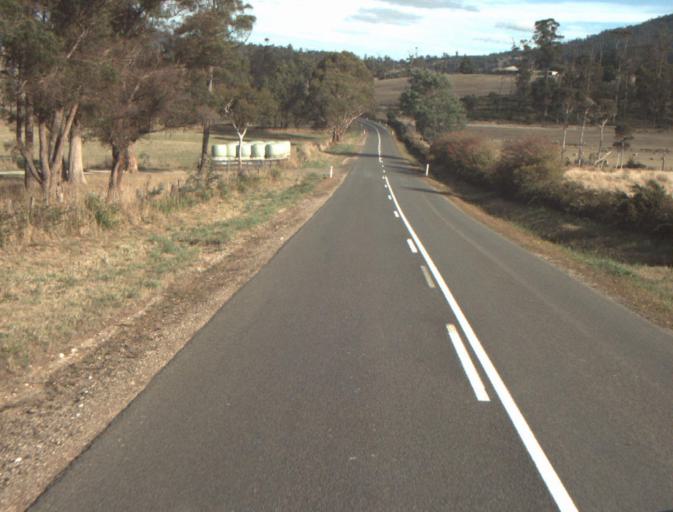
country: AU
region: Tasmania
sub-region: Launceston
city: Mayfield
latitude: -41.2209
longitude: 147.1216
